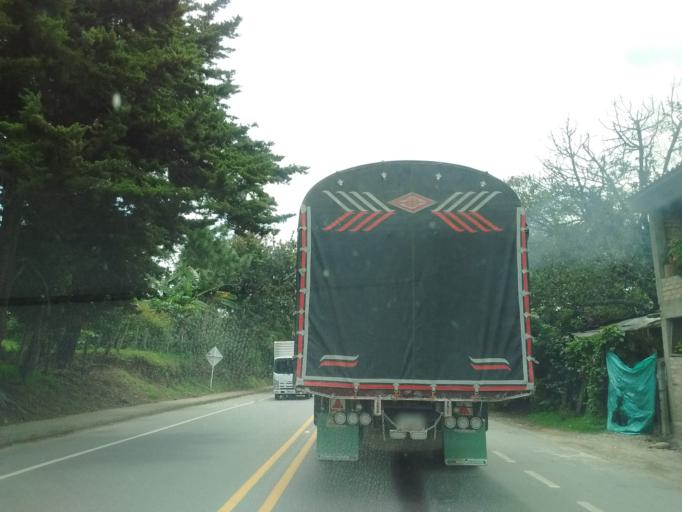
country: CO
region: Cauca
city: Cajibio
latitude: 2.5236
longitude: -76.5495
